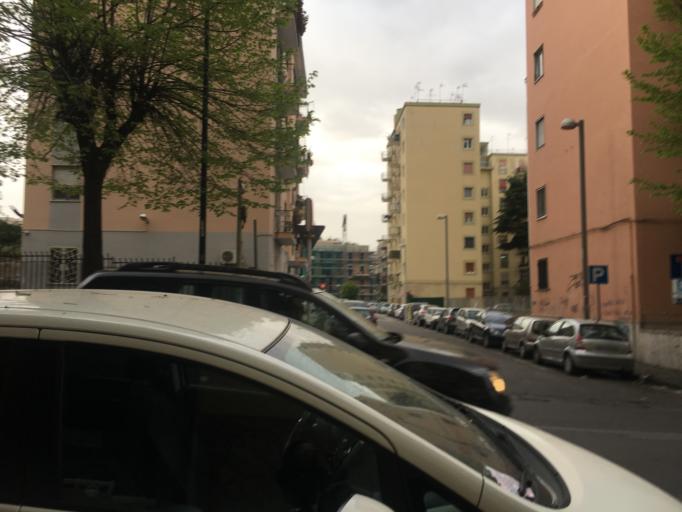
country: IT
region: Campania
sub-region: Provincia di Napoli
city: Napoli
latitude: 40.8537
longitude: 14.2256
